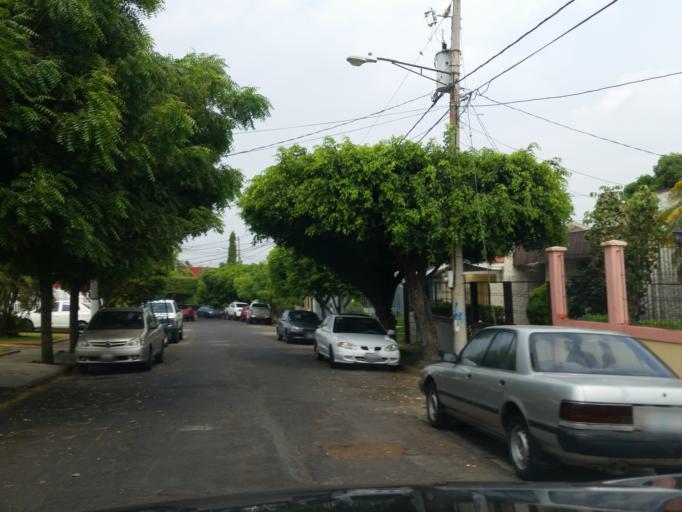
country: NI
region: Managua
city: Managua
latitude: 12.1170
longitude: -86.2529
